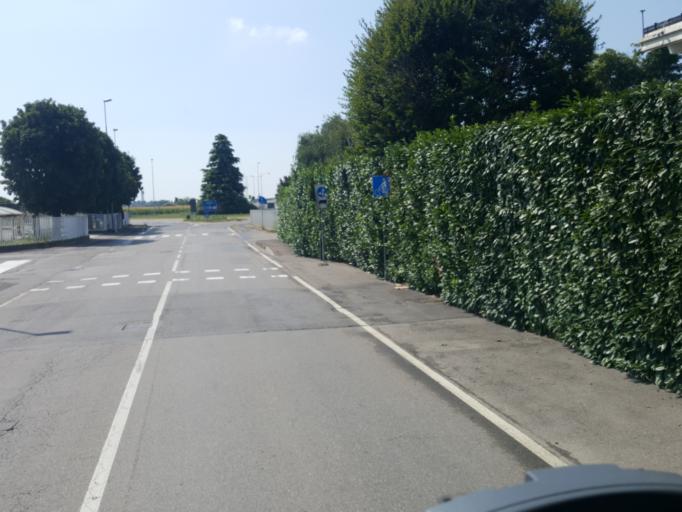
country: IT
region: Lombardy
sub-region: Provincia di Como
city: Turate
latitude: 45.6555
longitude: 9.0177
